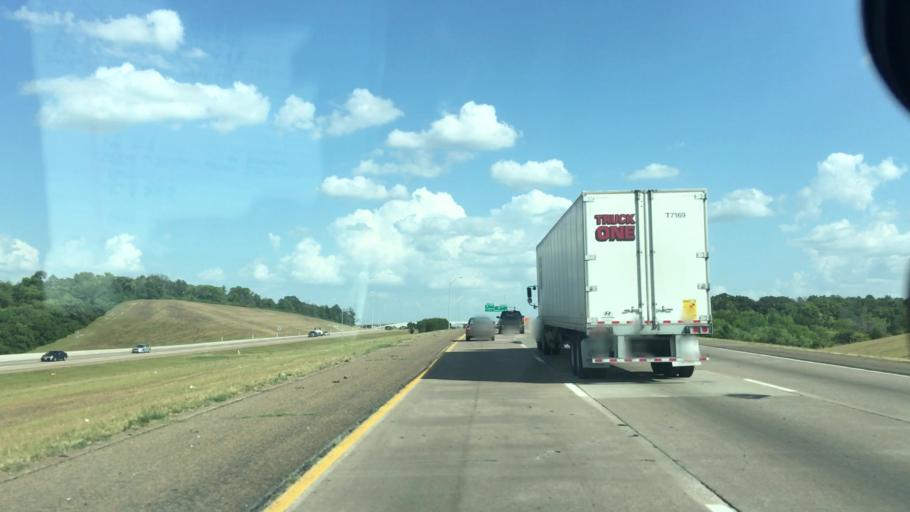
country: US
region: Texas
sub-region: Dallas County
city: Hutchins
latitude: 32.6698
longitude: -96.7342
